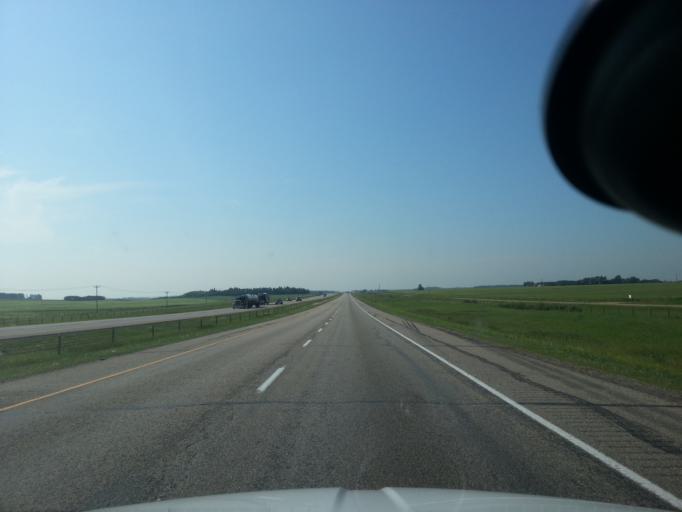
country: CA
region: Alberta
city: Olds
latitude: 51.8691
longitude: -114.0256
